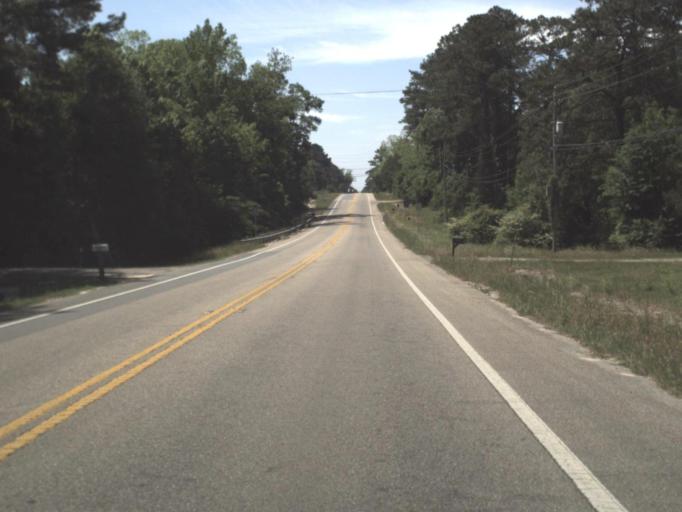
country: US
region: Florida
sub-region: Jackson County
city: Marianna
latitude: 30.7509
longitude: -85.2298
